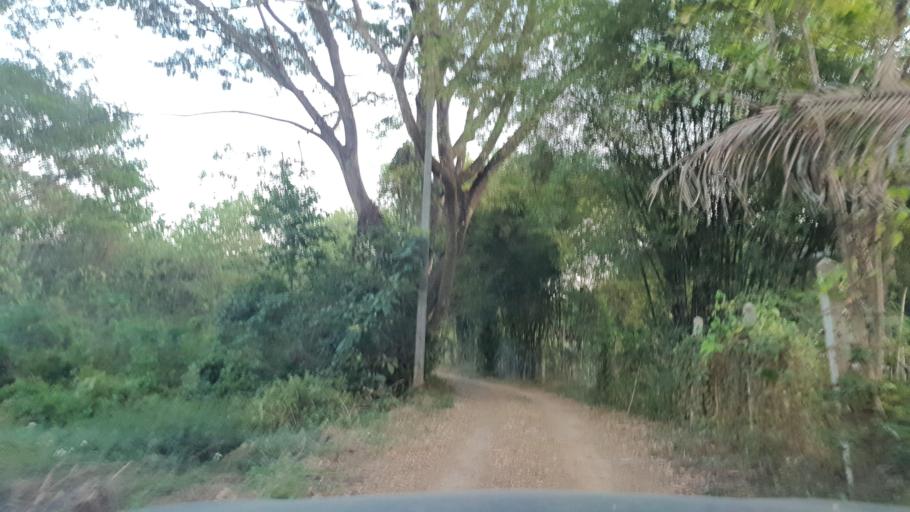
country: TH
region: Chiang Mai
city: Mae Wang
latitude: 18.6976
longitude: 98.8145
